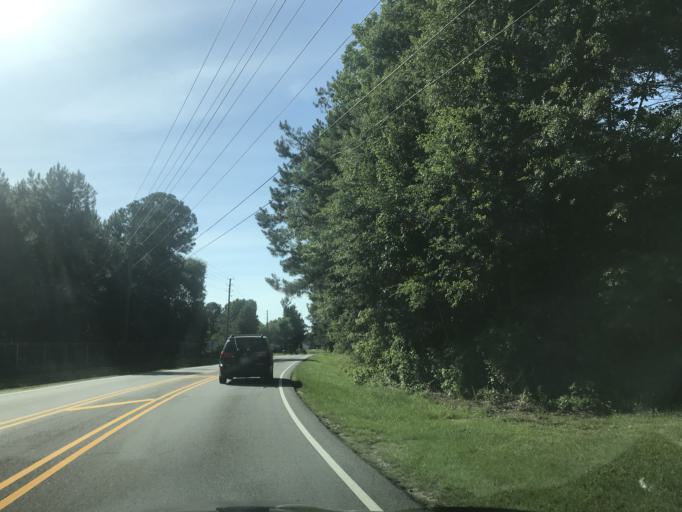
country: US
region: North Carolina
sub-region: Wake County
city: Garner
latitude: 35.6670
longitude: -78.5715
